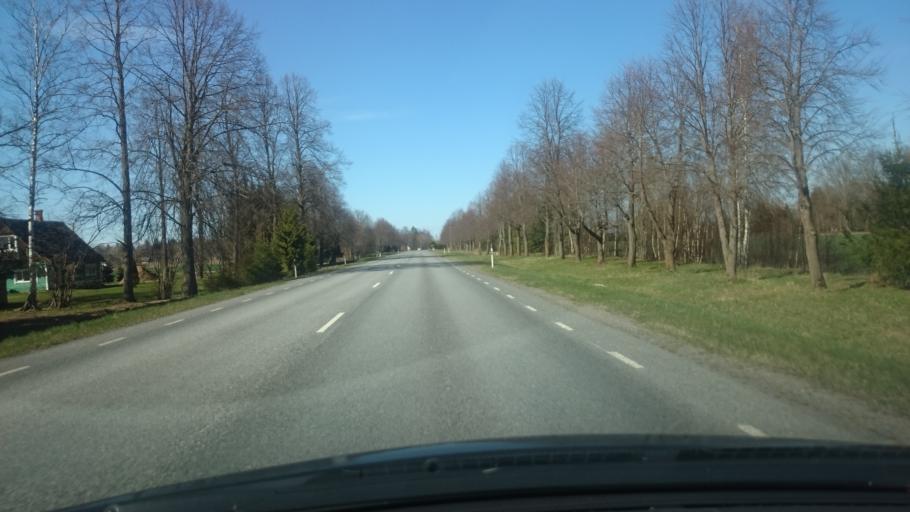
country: EE
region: Polvamaa
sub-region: Polva linn
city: Polva
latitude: 58.2574
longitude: 27.0028
